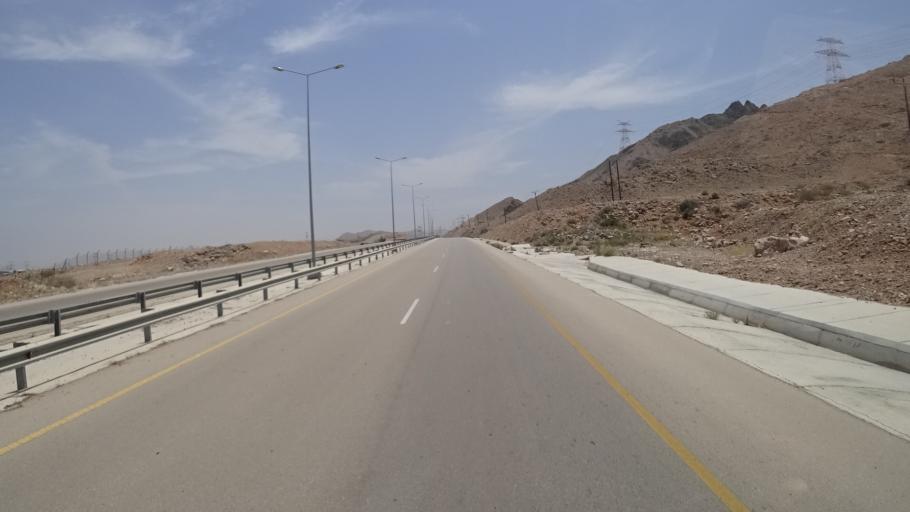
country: OM
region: Ash Sharqiyah
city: Sur
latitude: 22.6636
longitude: 59.3901
